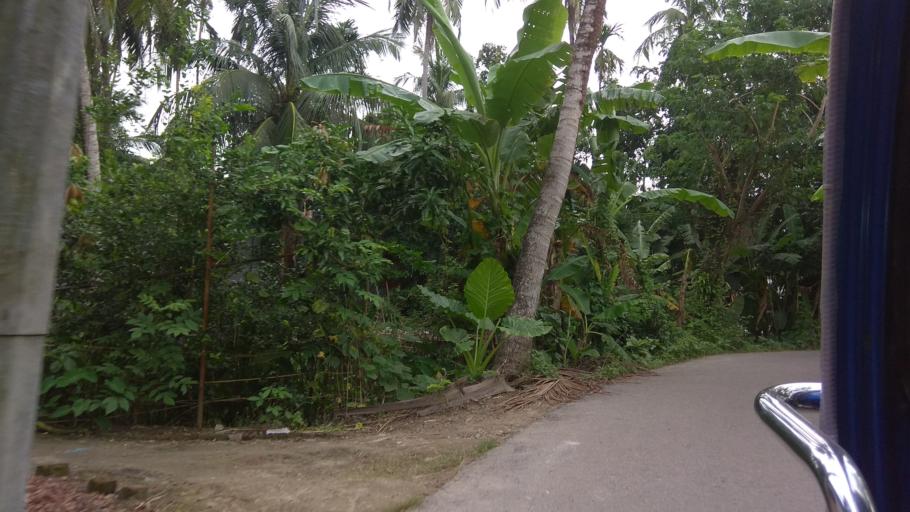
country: BD
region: Khulna
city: Kalia
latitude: 23.0315
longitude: 89.6553
